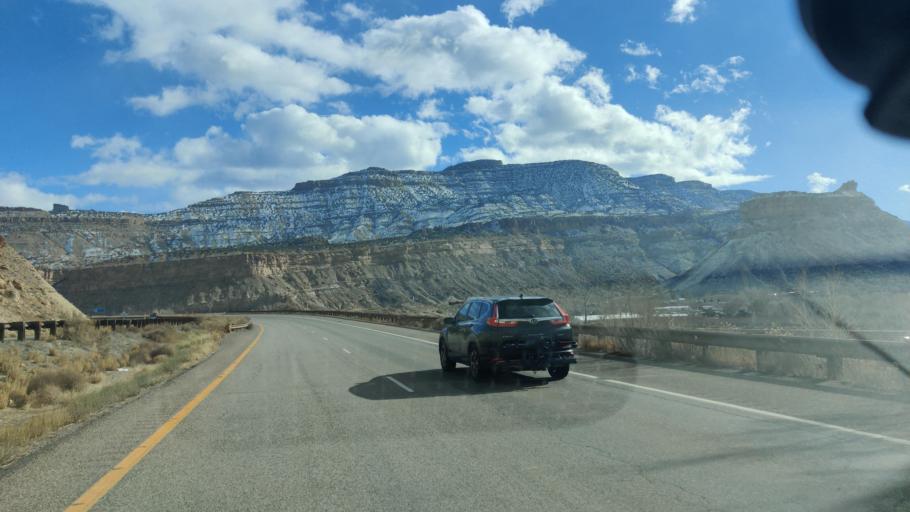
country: US
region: Colorado
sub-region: Mesa County
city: Palisade
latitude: 39.1195
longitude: -108.3355
